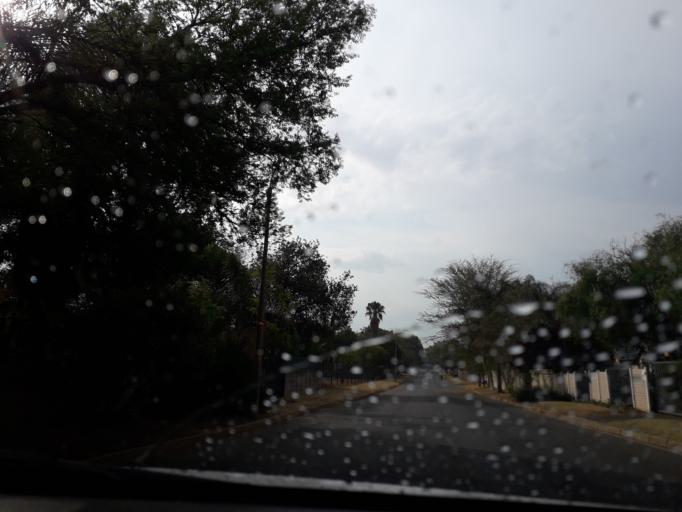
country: ZA
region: Gauteng
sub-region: City of Johannesburg Metropolitan Municipality
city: Modderfontein
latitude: -26.0930
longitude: 28.2468
